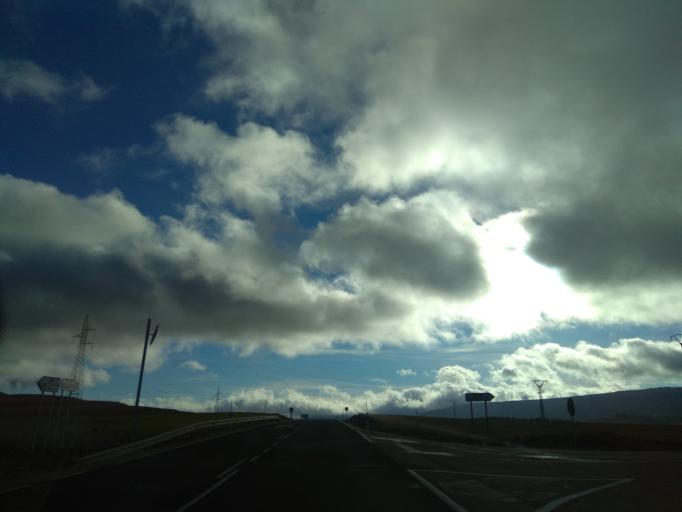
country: ES
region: Castille and Leon
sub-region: Provincia de Palencia
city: Pomar de Valdivia
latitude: 42.7499
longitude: -4.1681
